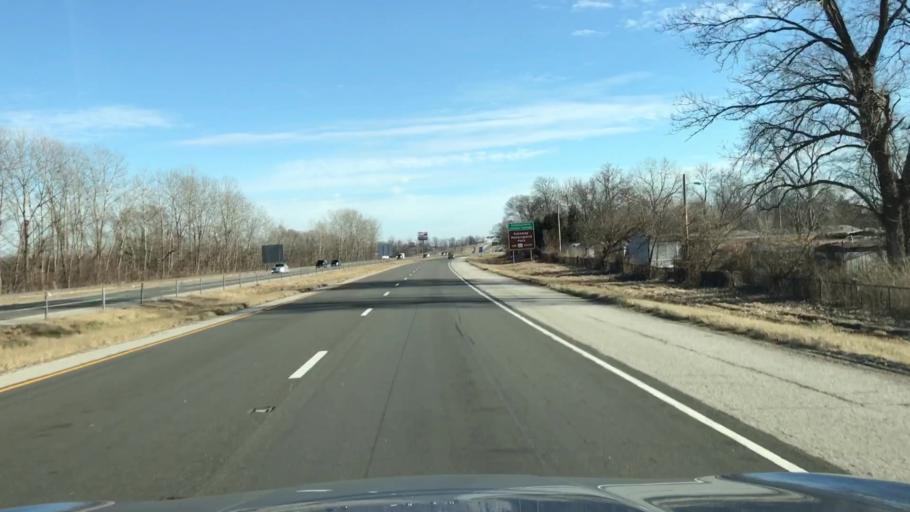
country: US
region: Illinois
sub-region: Madison County
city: Mitchell
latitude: 38.7647
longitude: -90.1093
